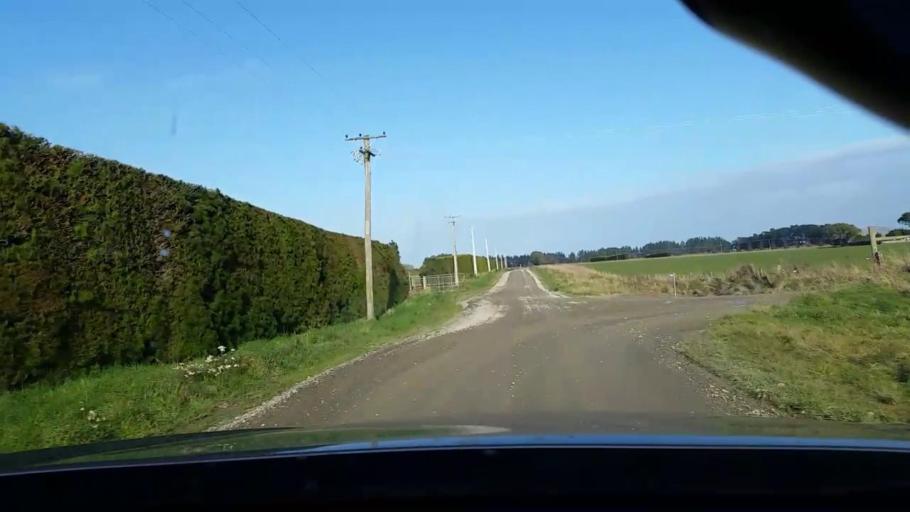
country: NZ
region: Southland
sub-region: Invercargill City
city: Invercargill
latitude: -46.2904
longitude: 168.2947
